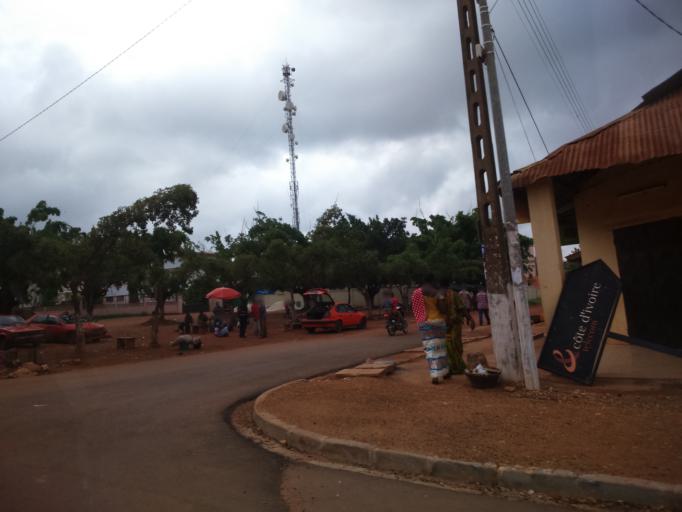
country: CI
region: Moyen-Comoe
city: Abengourou
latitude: 6.7291
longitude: -3.4866
